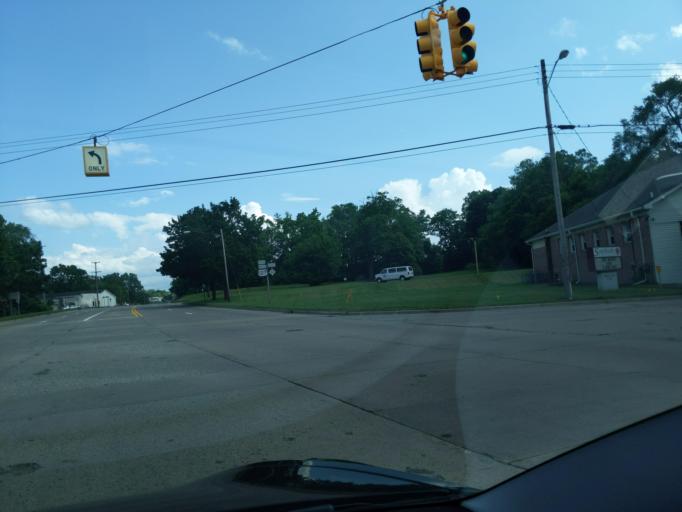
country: US
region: Michigan
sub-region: Jackson County
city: Jackson
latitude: 42.2331
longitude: -84.3927
